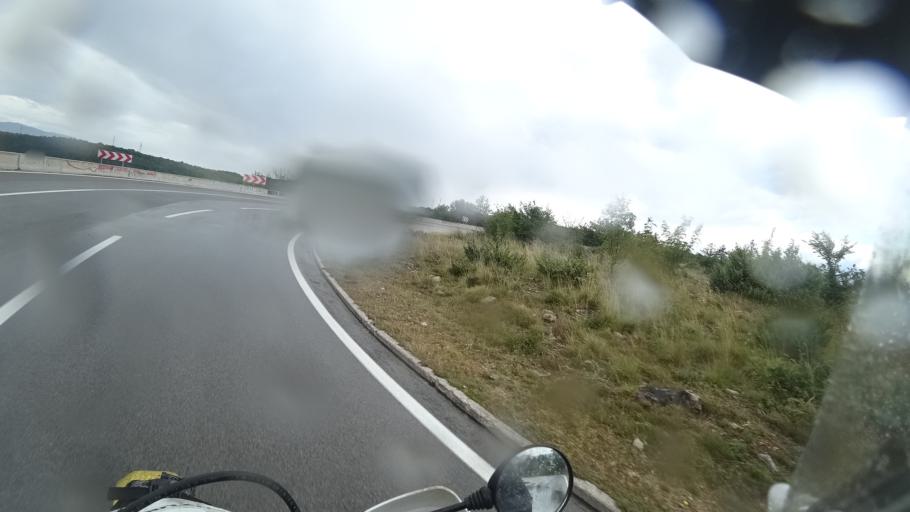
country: HR
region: Sibensko-Kniniska
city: Knin
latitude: 44.0407
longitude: 16.1842
